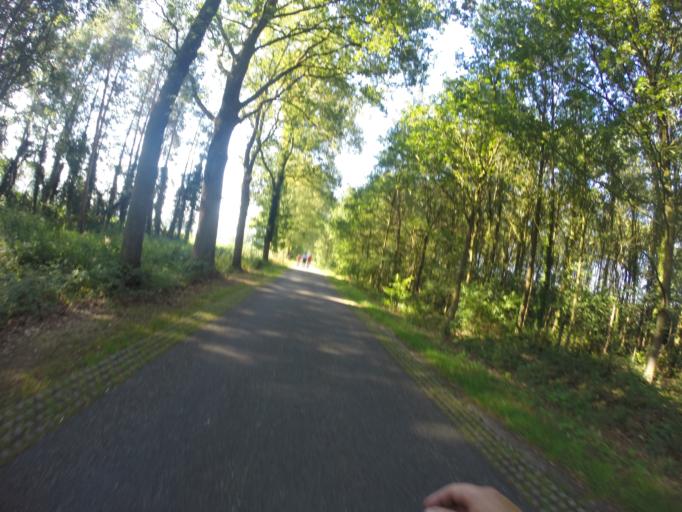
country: NL
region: Gelderland
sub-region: Gemeente Bronckhorst
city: Hengelo
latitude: 52.0898
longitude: 6.3478
